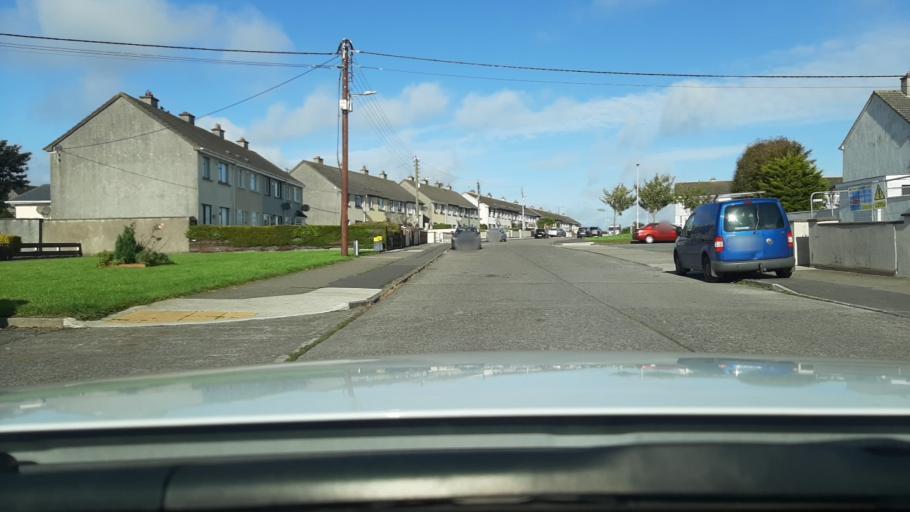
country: IE
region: Leinster
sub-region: Kildare
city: Kildare
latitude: 53.1609
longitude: -6.9042
